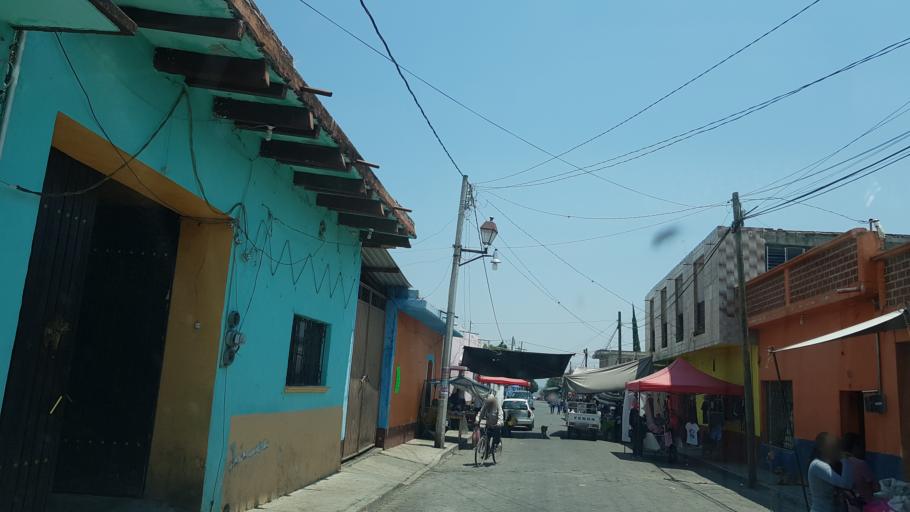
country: MX
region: Puebla
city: Huaquechula
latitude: 18.7691
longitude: -98.5437
